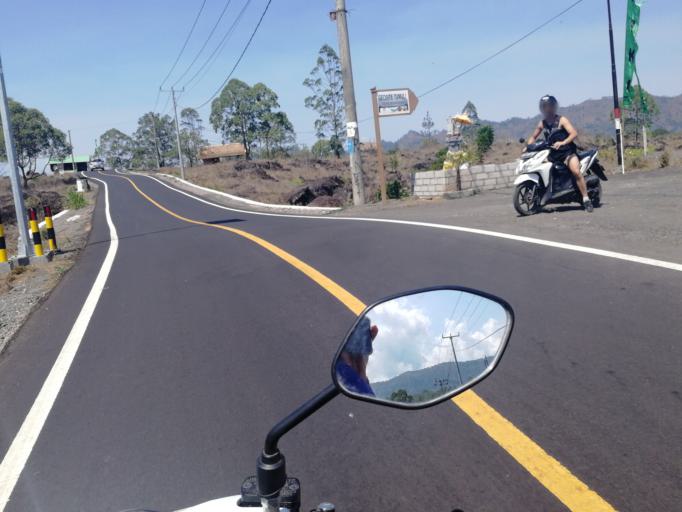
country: ID
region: Bali
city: Banjar Kedisan
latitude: -8.2584
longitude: 115.3922
